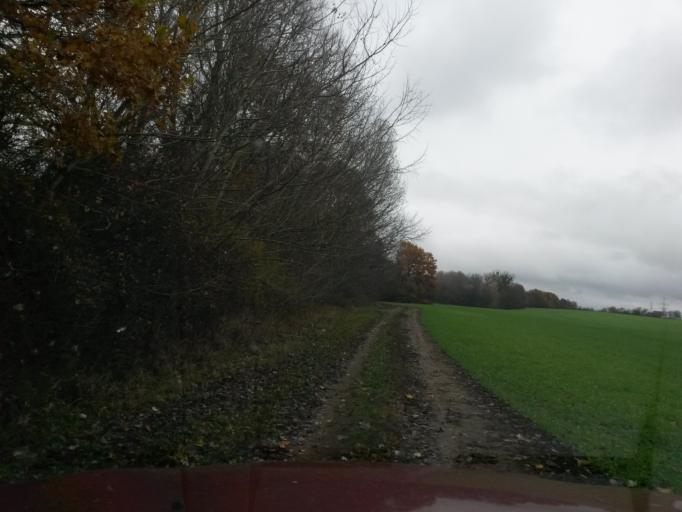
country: SK
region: Kosicky
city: Michalovce
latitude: 48.5637
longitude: 21.9436
